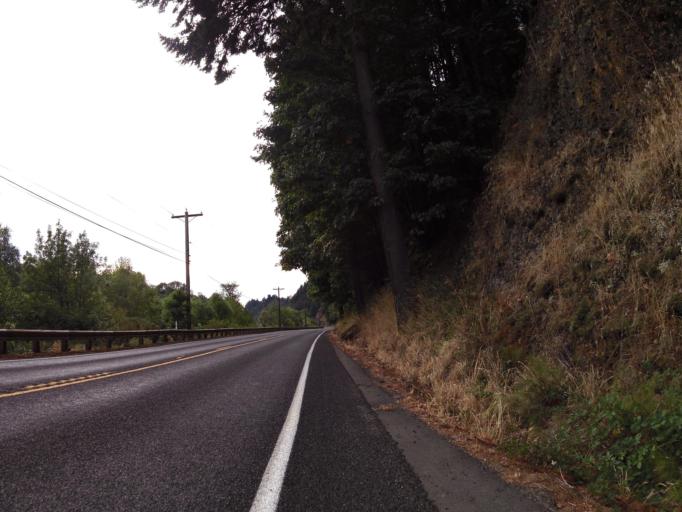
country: US
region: Washington
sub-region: Cowlitz County
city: West Longview
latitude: 46.1892
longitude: -123.1069
